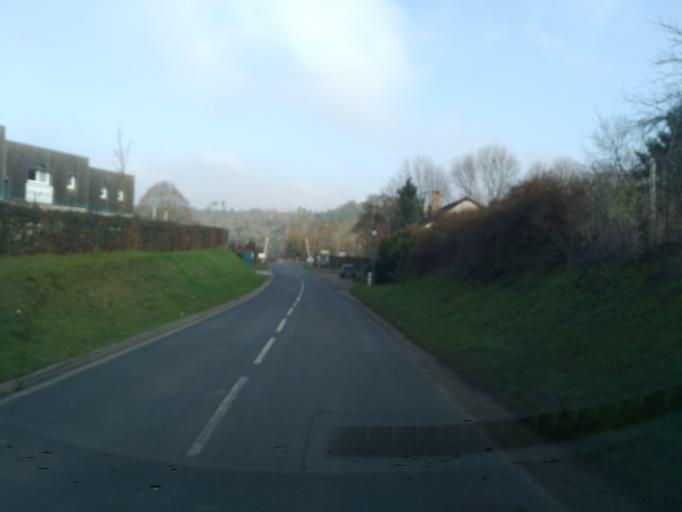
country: FR
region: Ile-de-France
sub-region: Departement des Yvelines
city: Saint-Germain-de-la-Grange
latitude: 48.8365
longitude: 1.9049
